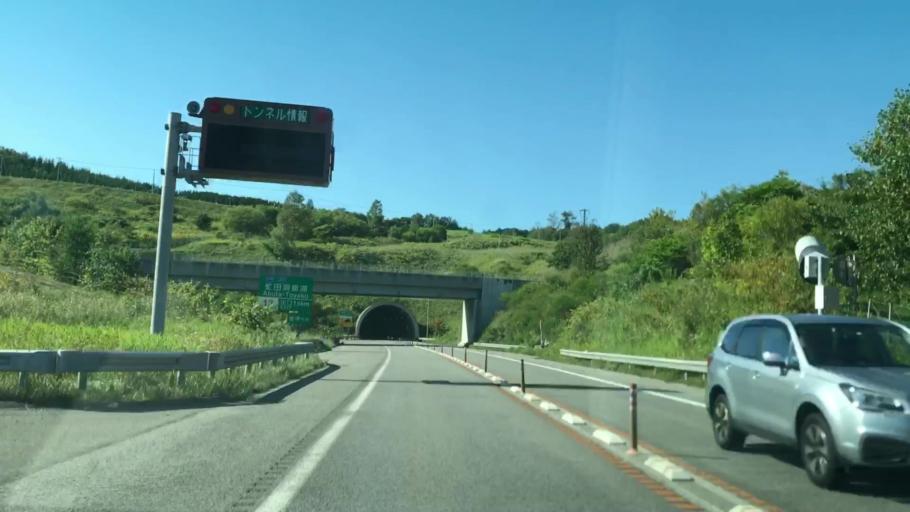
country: JP
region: Hokkaido
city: Date
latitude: 42.5512
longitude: 140.7894
